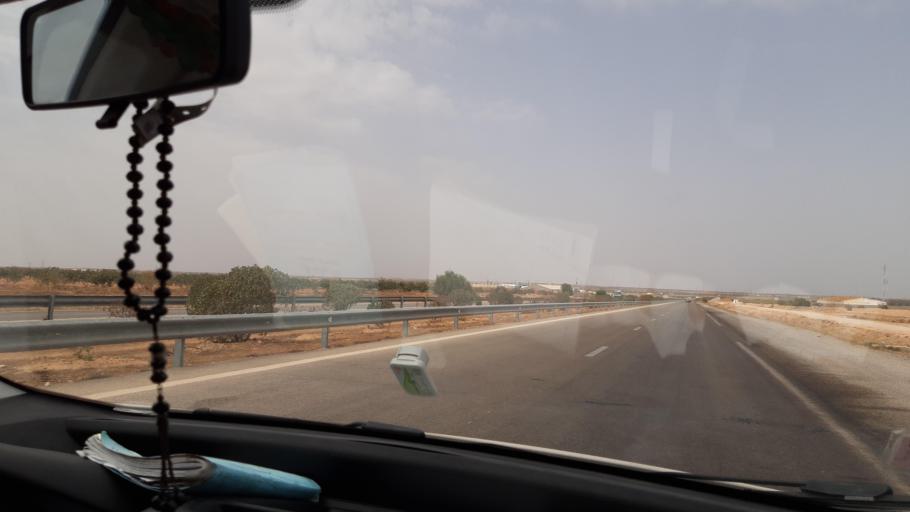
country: TN
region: Safaqis
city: Sfax
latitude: 34.8674
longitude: 10.6915
